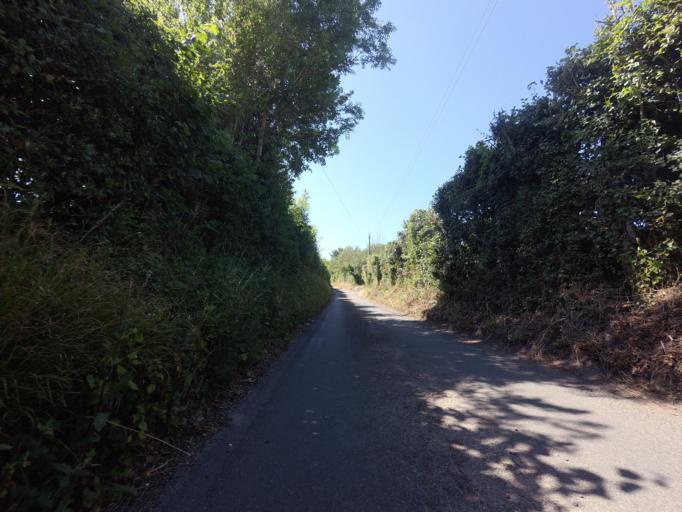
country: GB
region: England
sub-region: Kent
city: Swanley
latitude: 51.4091
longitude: 0.2053
